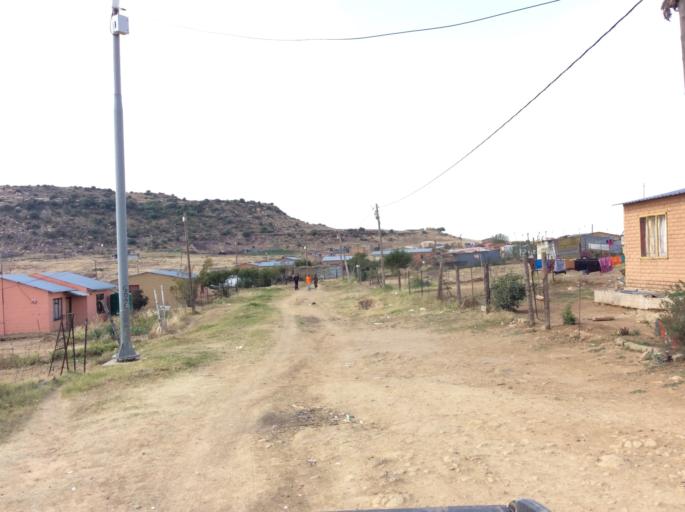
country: ZA
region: Orange Free State
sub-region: Xhariep District Municipality
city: Dewetsdorp
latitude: -29.5932
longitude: 26.6820
